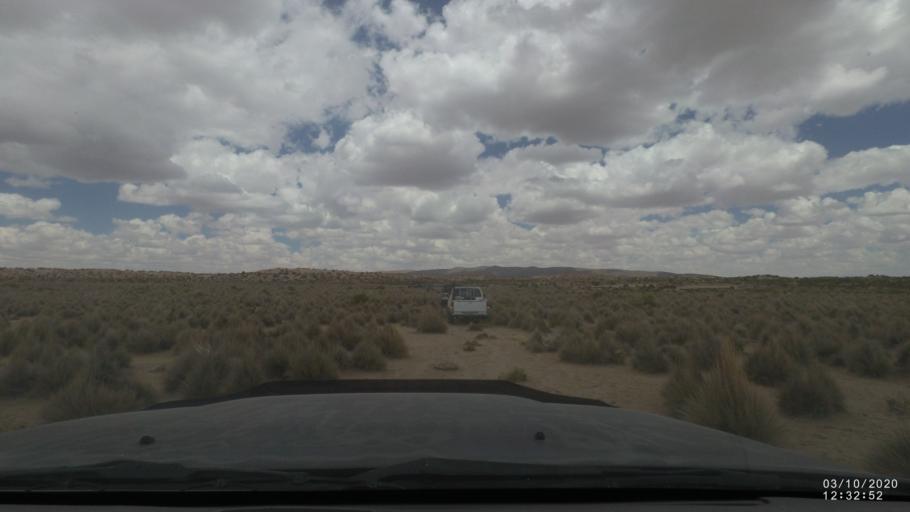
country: BO
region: Oruro
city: Poopo
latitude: -18.6880
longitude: -67.5358
